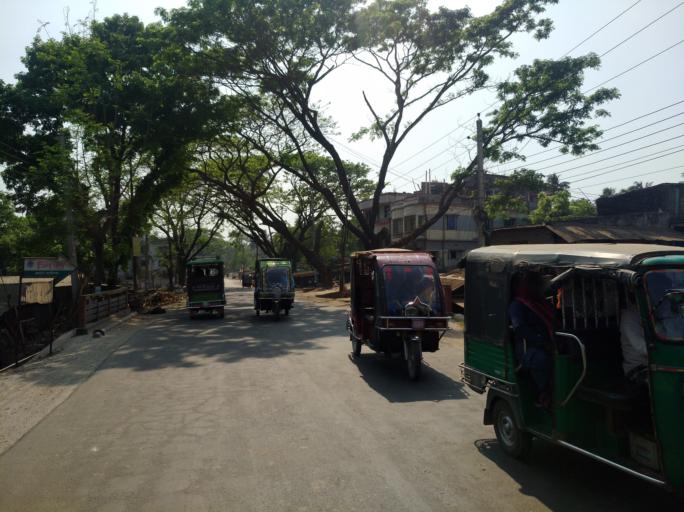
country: BD
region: Khulna
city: Kaliganj
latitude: 23.5493
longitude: 89.1683
